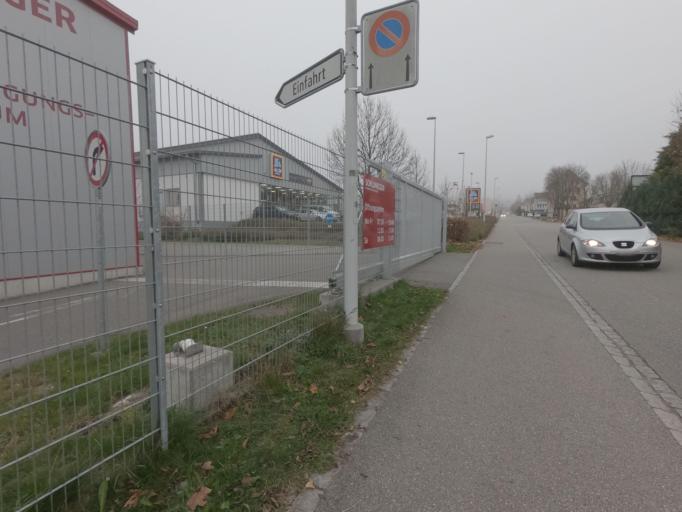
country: CH
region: Solothurn
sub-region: Bezirk Lebern
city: Grenchen
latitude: 47.1928
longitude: 7.4080
